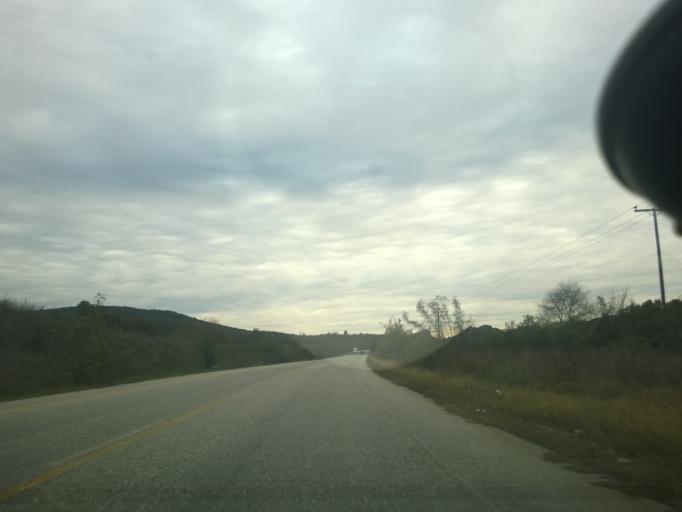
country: GR
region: Central Macedonia
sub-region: Nomos Pellis
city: Apsalos
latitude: 40.8585
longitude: 22.1032
